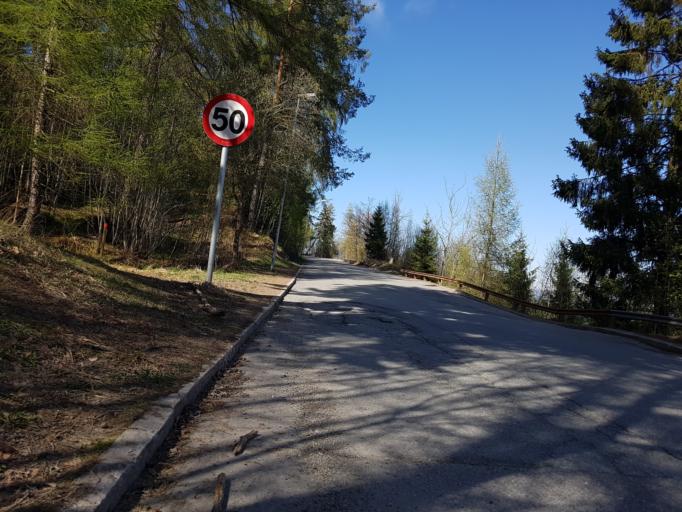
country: NO
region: Sor-Trondelag
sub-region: Trondheim
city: Trondheim
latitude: 63.4291
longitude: 10.3555
